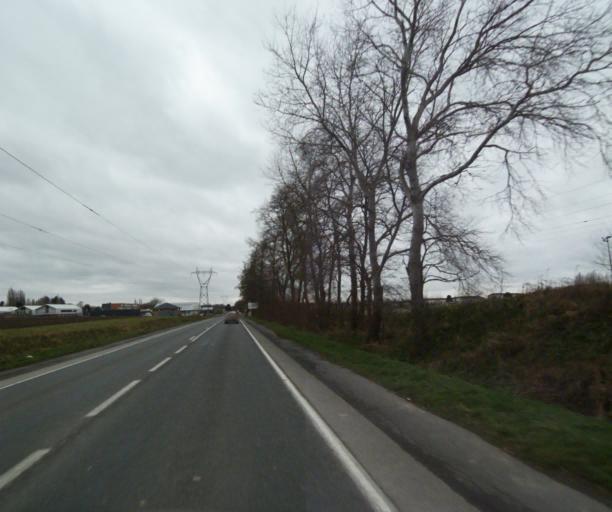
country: FR
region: Nord-Pas-de-Calais
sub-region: Departement du Nord
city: Marly
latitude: 50.3485
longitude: 3.5561
